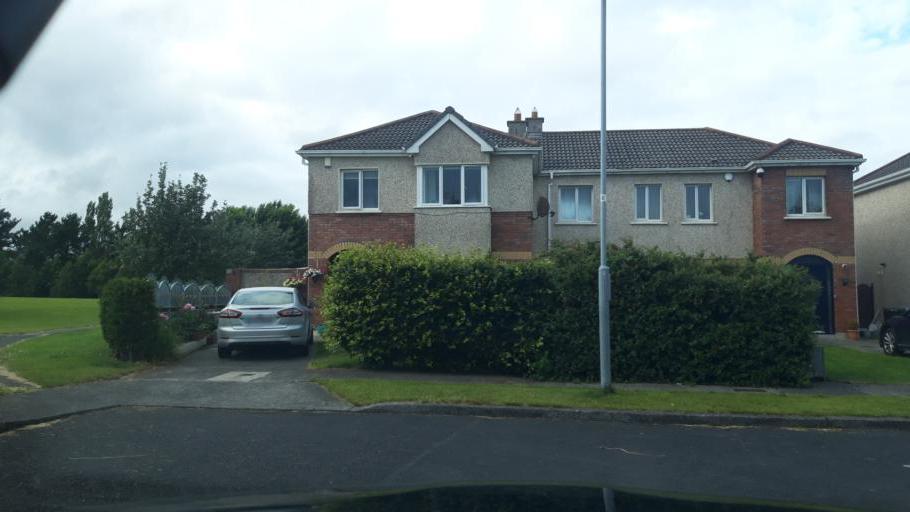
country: IE
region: Leinster
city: Hartstown
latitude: 53.4058
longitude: -6.4191
